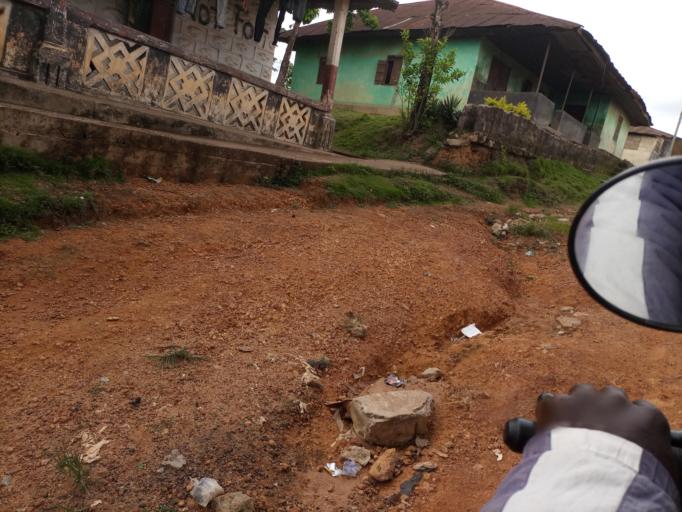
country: SL
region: Southern Province
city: Bo
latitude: 7.9522
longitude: -11.7325
